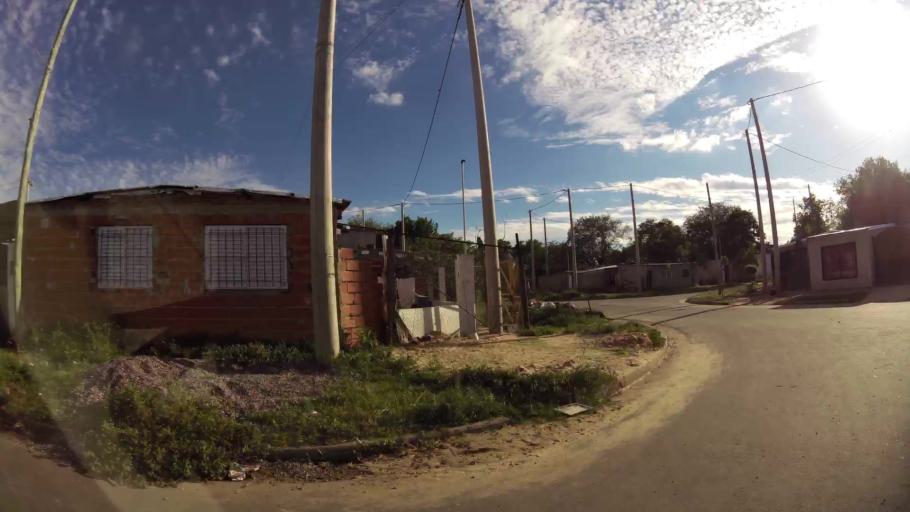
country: AR
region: Santa Fe
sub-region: Departamento de Rosario
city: Rosario
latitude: -32.9855
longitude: -60.6694
